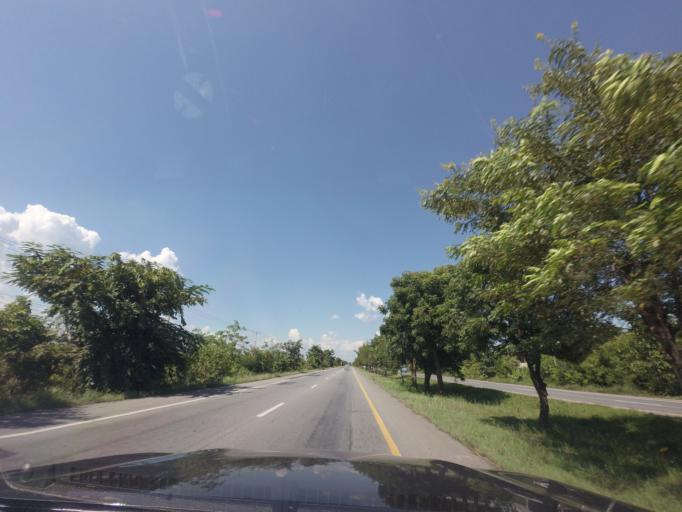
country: TH
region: Nakhon Ratchasima
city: Non Sung
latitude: 15.2139
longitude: 102.3581
